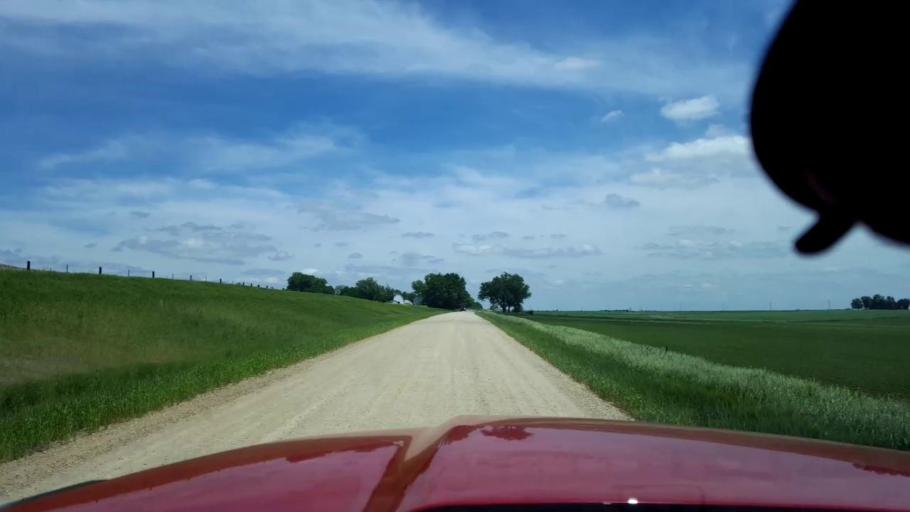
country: US
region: Iowa
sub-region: Linn County
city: Lisbon
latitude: 41.9560
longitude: -91.3647
